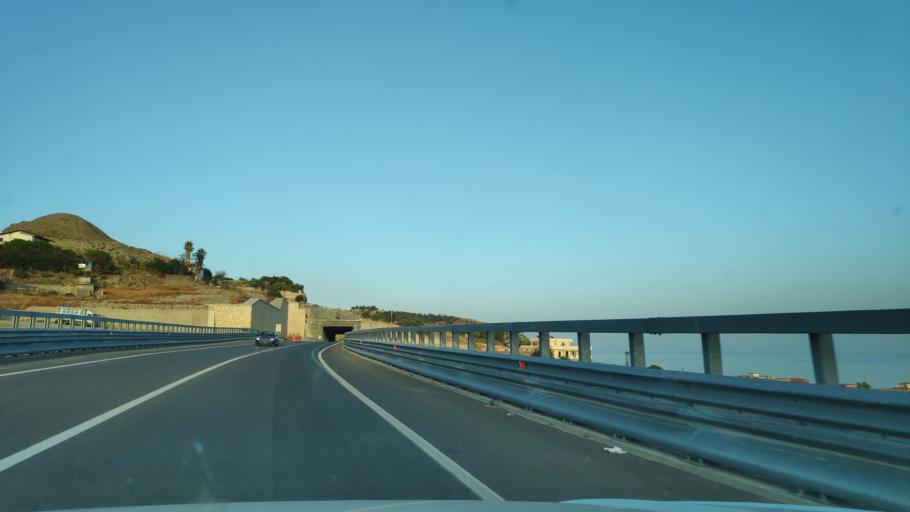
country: IT
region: Calabria
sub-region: Provincia di Reggio Calabria
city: Bova Marina
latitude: 37.9349
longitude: 15.9177
